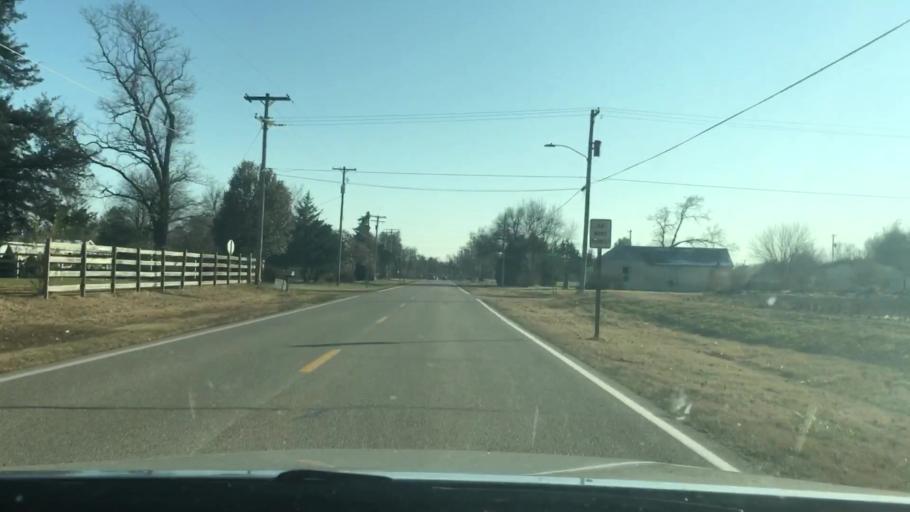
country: US
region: Kansas
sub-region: Reno County
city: Nickerson
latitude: 38.1556
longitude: -98.0874
